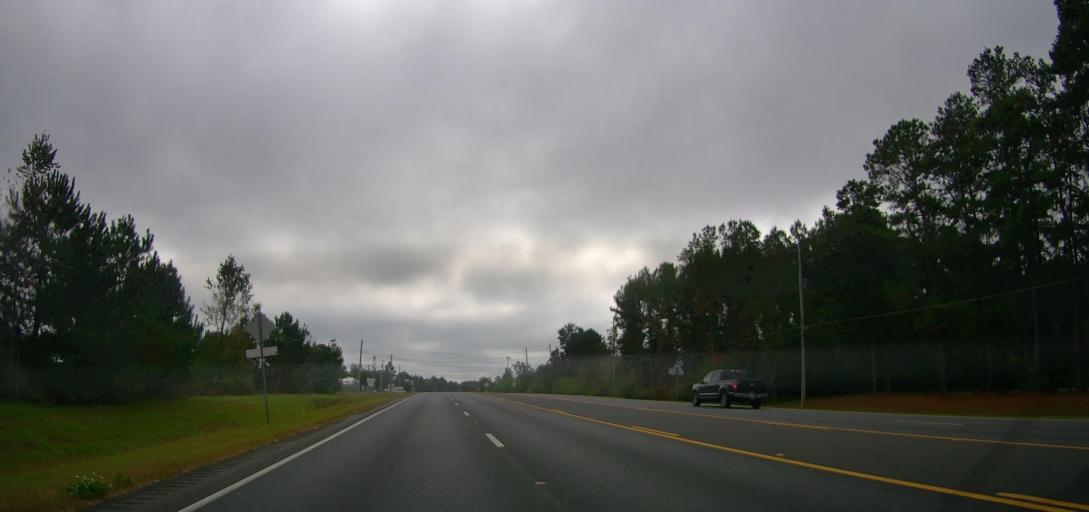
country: US
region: Georgia
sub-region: Thomas County
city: Thomasville
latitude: 30.8859
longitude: -83.9316
